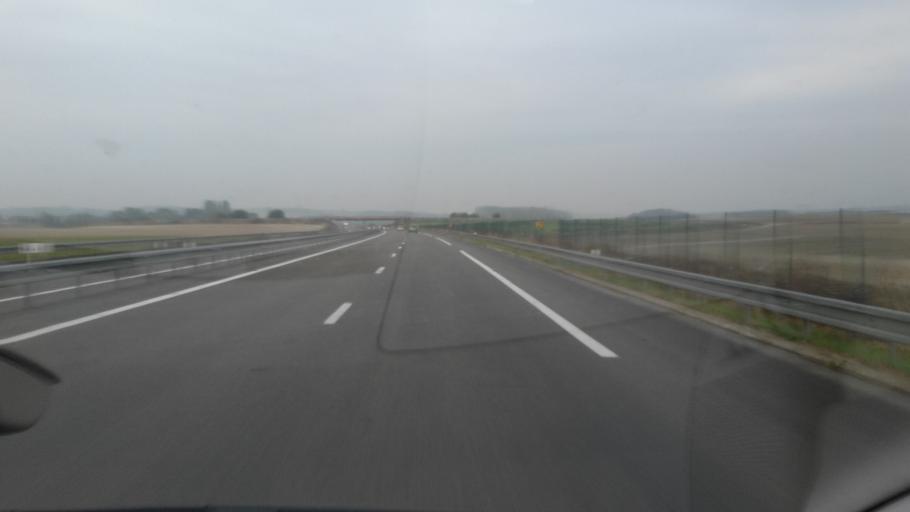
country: FR
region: Champagne-Ardenne
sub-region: Departement des Ardennes
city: Rethel
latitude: 49.5511
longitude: 4.4464
